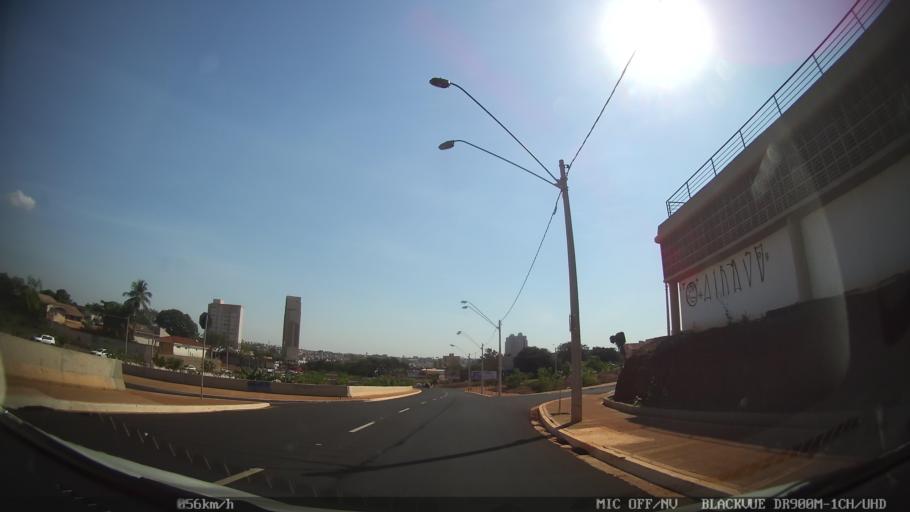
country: BR
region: Sao Paulo
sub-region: Ribeirao Preto
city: Ribeirao Preto
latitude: -21.2045
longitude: -47.8180
